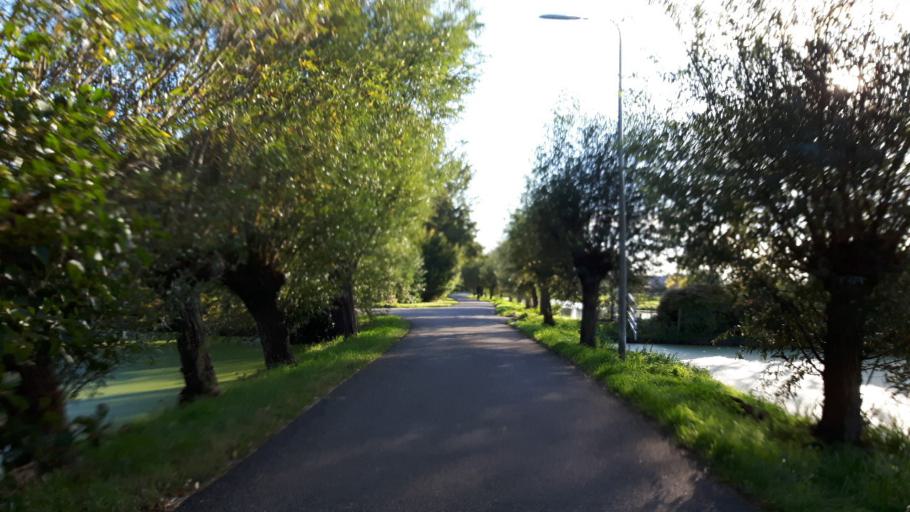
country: NL
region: Utrecht
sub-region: Gemeente Woerden
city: Woerden
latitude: 52.0571
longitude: 4.8677
